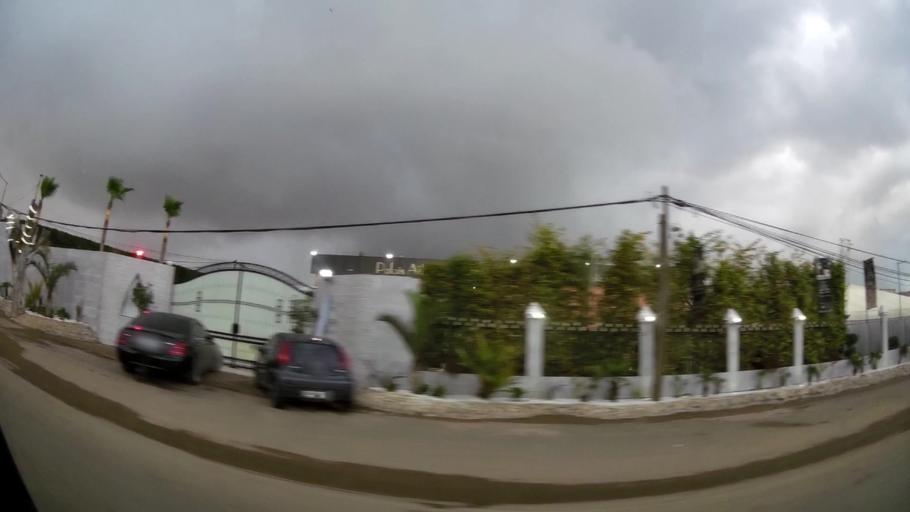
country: MA
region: Grand Casablanca
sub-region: Mediouna
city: Tit Mellil
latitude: 33.5677
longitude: -7.5114
